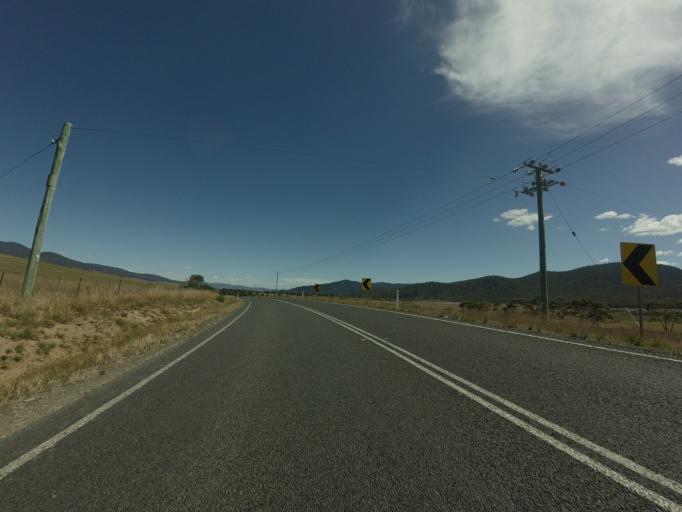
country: AU
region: Tasmania
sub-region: Break O'Day
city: St Helens
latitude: -41.6942
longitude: 147.8650
